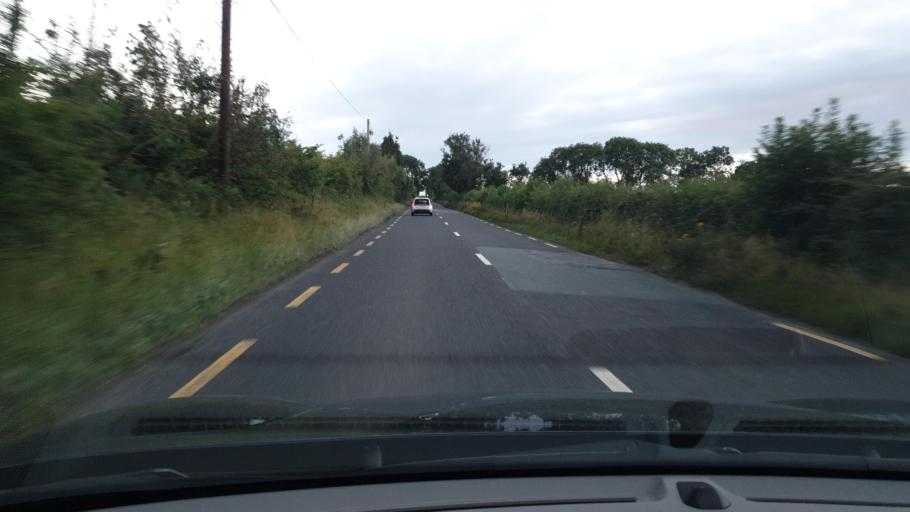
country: IE
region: Leinster
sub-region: An Mhi
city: Duleek
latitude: 53.6124
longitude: -6.4297
